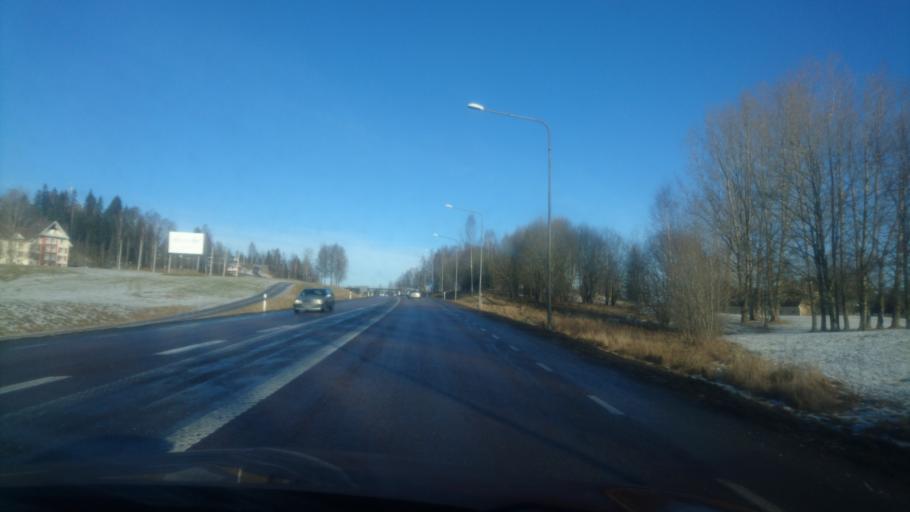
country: SE
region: Vaermland
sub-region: Sunne Kommun
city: Sunne
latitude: 59.8267
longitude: 13.1326
